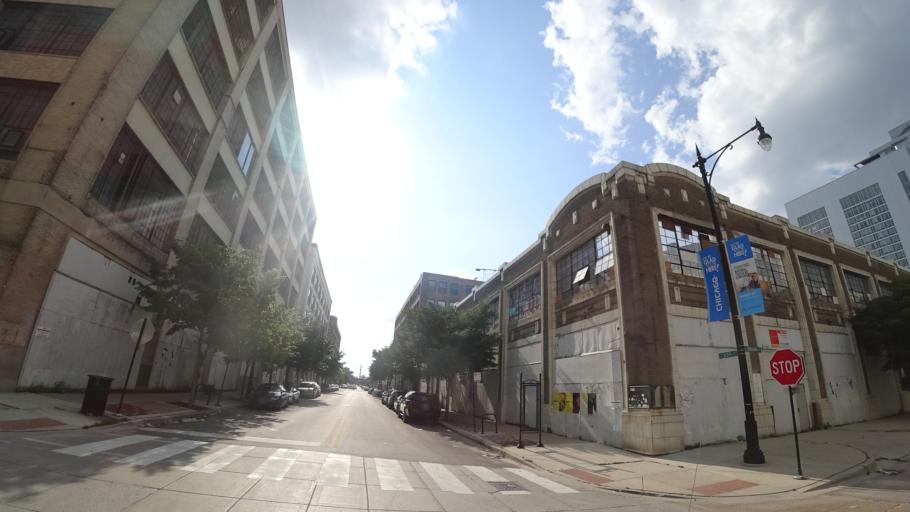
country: US
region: Illinois
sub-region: Cook County
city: Chicago
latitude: 41.8511
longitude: -87.6222
